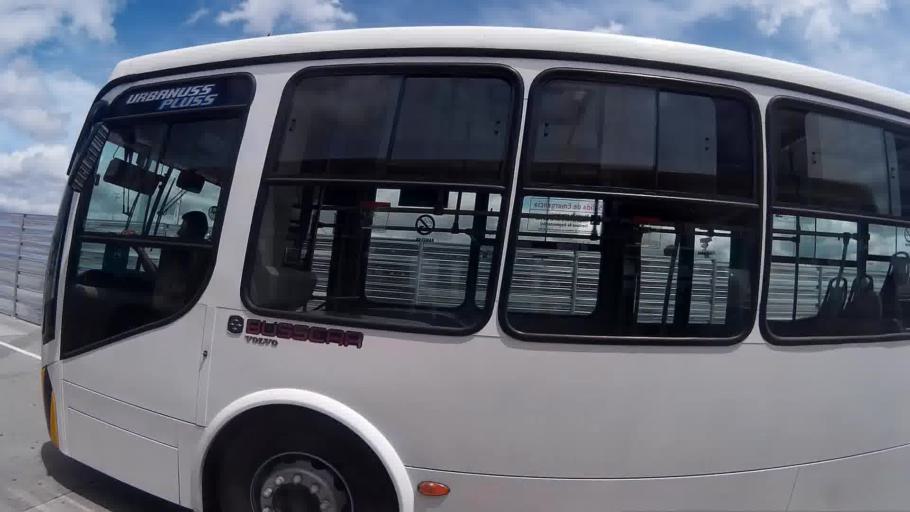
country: CO
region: Cundinamarca
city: Funza
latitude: 4.6968
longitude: -74.1373
